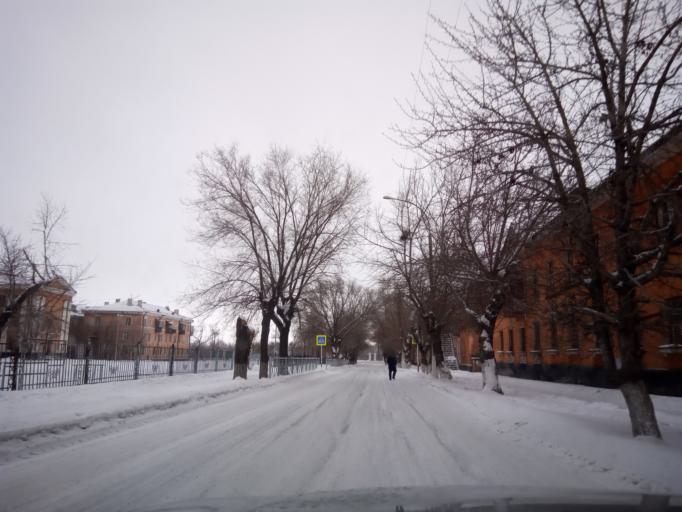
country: RU
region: Orenburg
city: Novotroitsk
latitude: 51.1972
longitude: 58.3270
